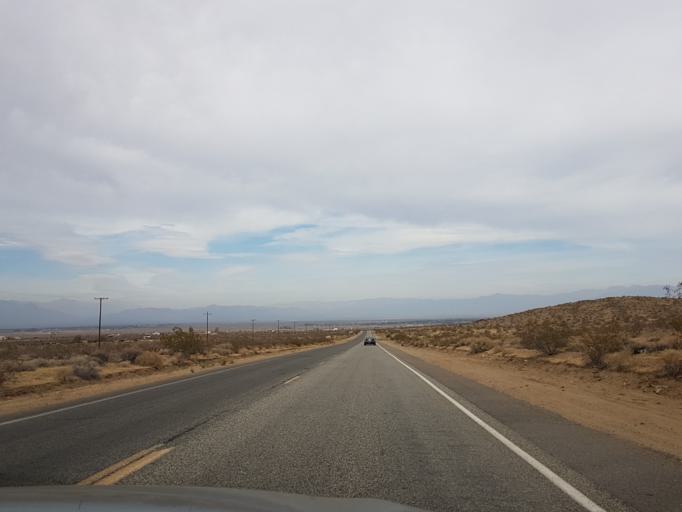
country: US
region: California
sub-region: Kern County
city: Ridgecrest
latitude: 35.5592
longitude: -117.7137
